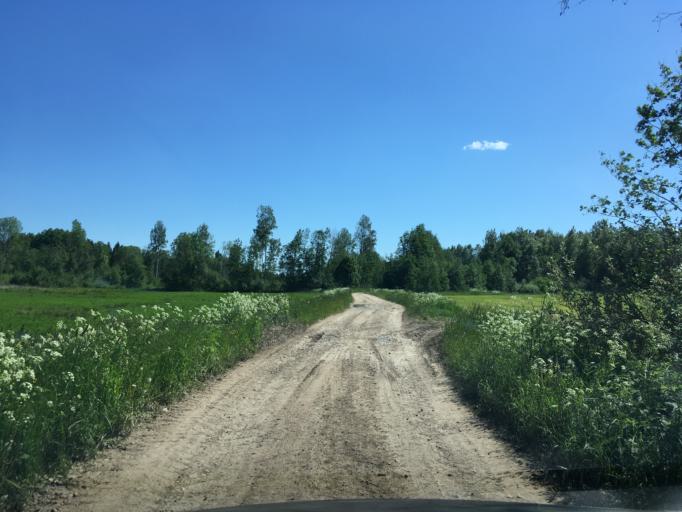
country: EE
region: Harju
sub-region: Rae vald
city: Vaida
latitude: 59.1577
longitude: 25.1334
